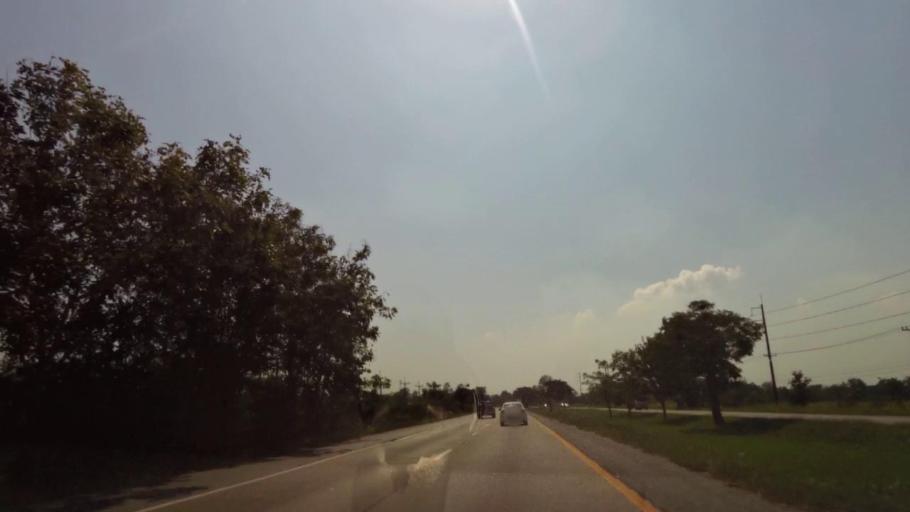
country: TH
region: Phichit
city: Wachira Barami
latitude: 16.5916
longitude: 100.1469
